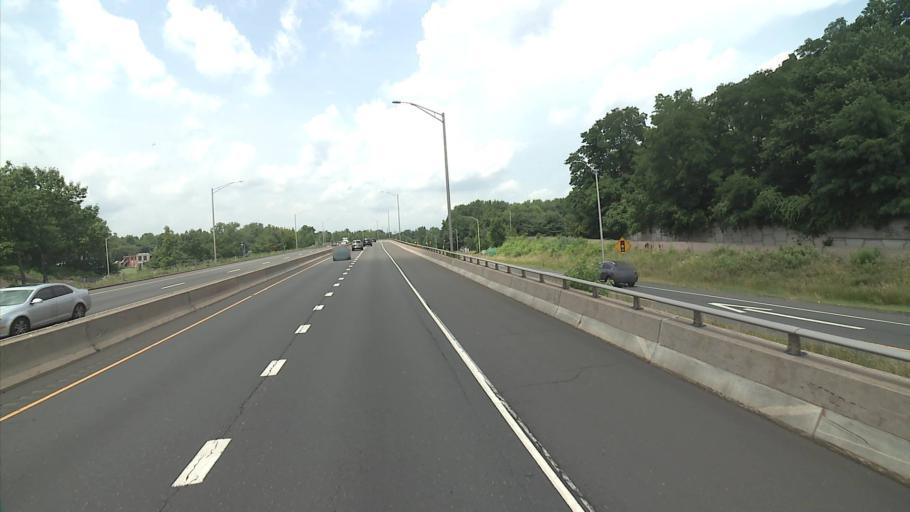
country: US
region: Connecticut
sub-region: Hartford County
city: South Windsor
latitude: 41.8163
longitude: -72.6536
